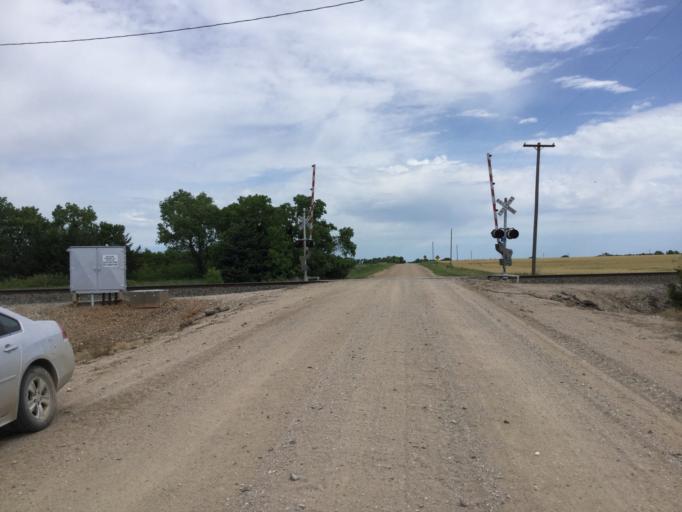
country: US
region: Kansas
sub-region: Marion County
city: Peabody
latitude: 38.1539
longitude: -97.2088
